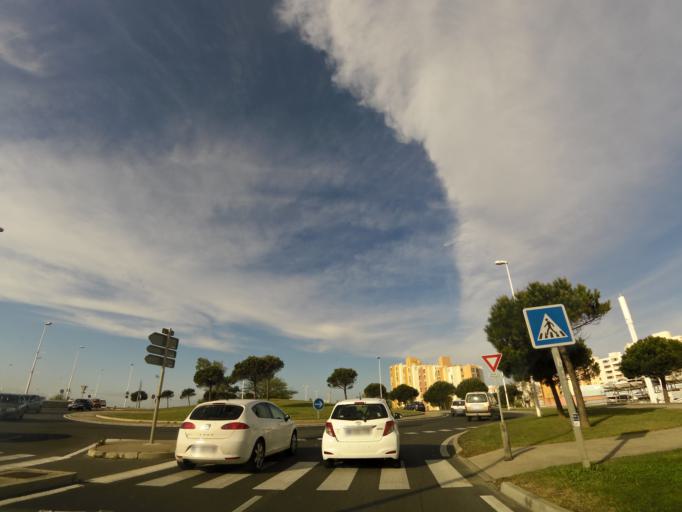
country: FR
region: Languedoc-Roussillon
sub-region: Departement de l'Herault
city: Perols
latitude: 43.5456
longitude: 3.9707
